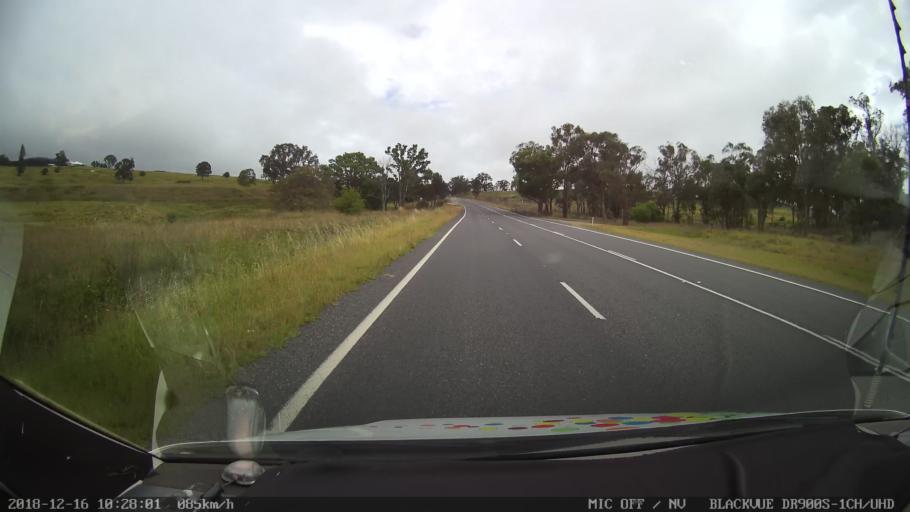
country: AU
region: New South Wales
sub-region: Tenterfield Municipality
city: Carrolls Creek
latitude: -29.1264
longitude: 151.9969
